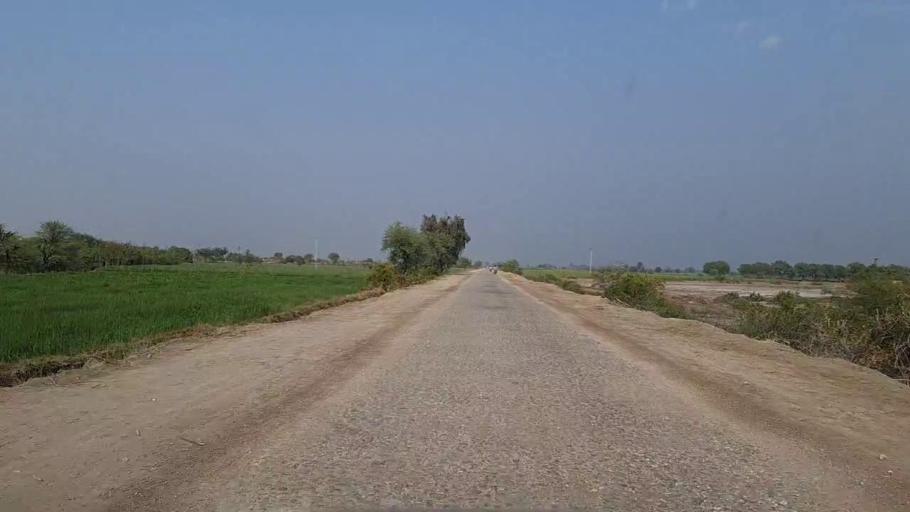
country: PK
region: Sindh
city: Mirwah Gorchani
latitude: 25.4108
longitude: 69.1426
